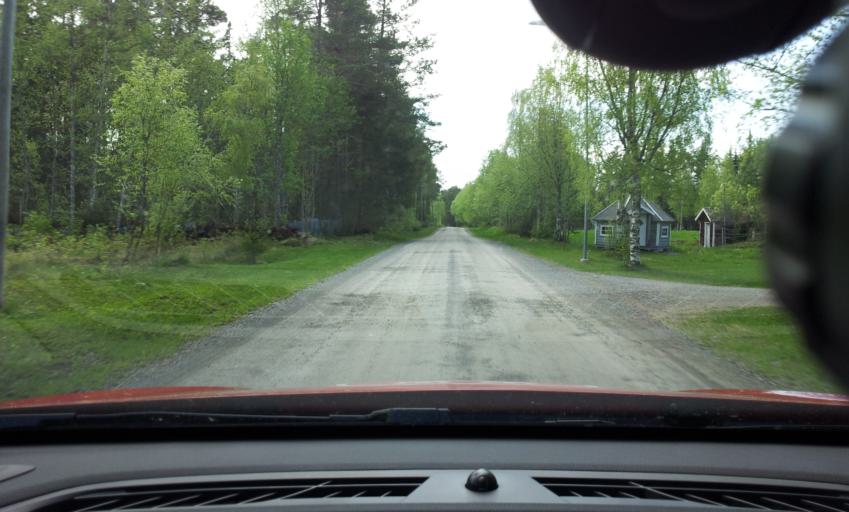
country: SE
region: Jaemtland
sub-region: Bergs Kommun
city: Hoverberg
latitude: 62.9391
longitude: 14.5163
